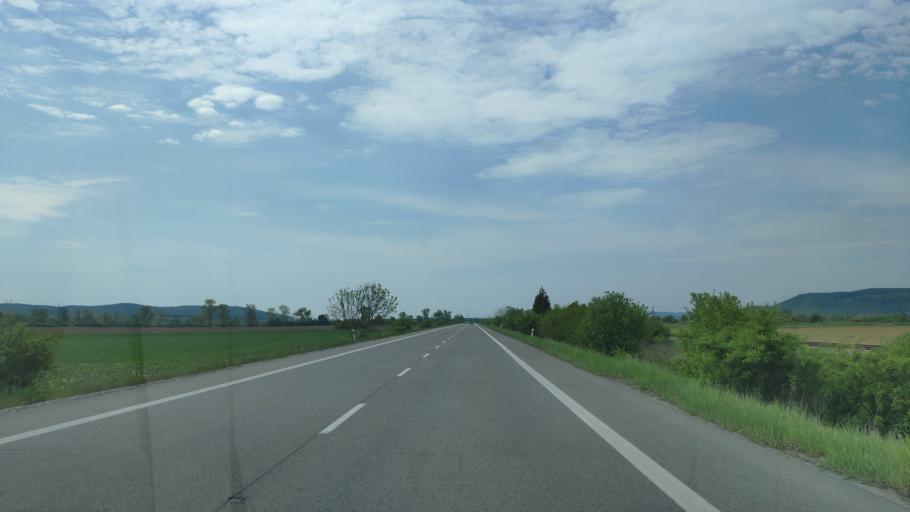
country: HU
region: Borsod-Abauj-Zemplen
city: Putnok
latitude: 48.4693
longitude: 20.3525
